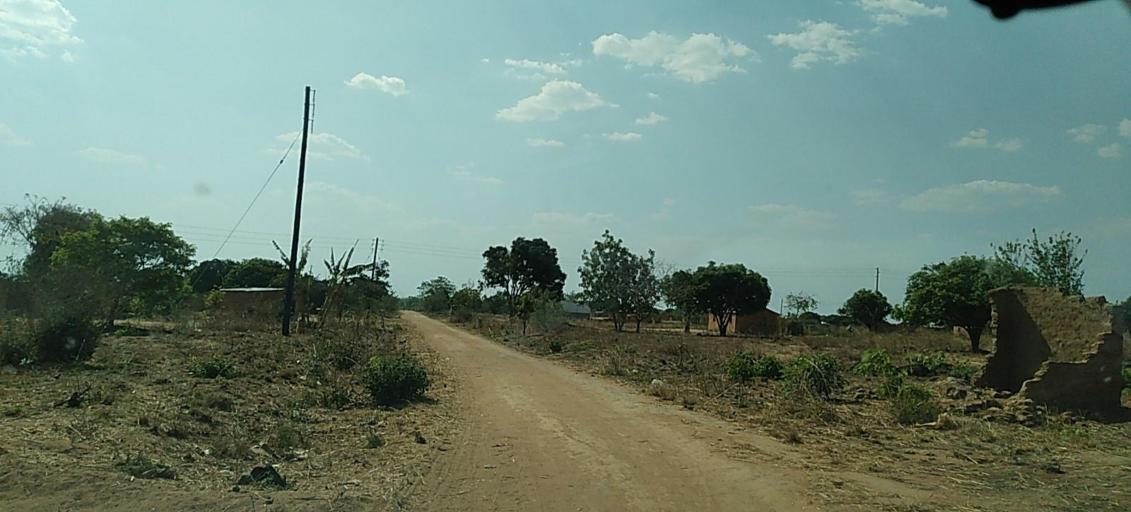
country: ZM
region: North-Western
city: Kalengwa
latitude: -13.1251
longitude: 25.0072
